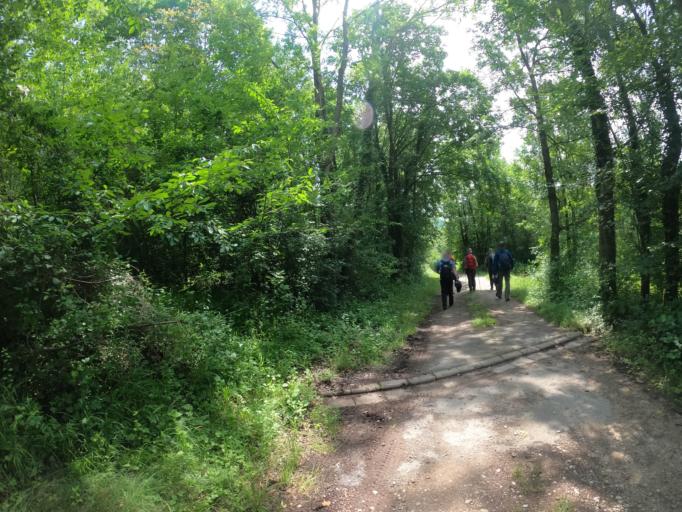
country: DE
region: Bavaria
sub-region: Upper Franconia
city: Poxdorf
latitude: 49.9216
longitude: 11.0751
